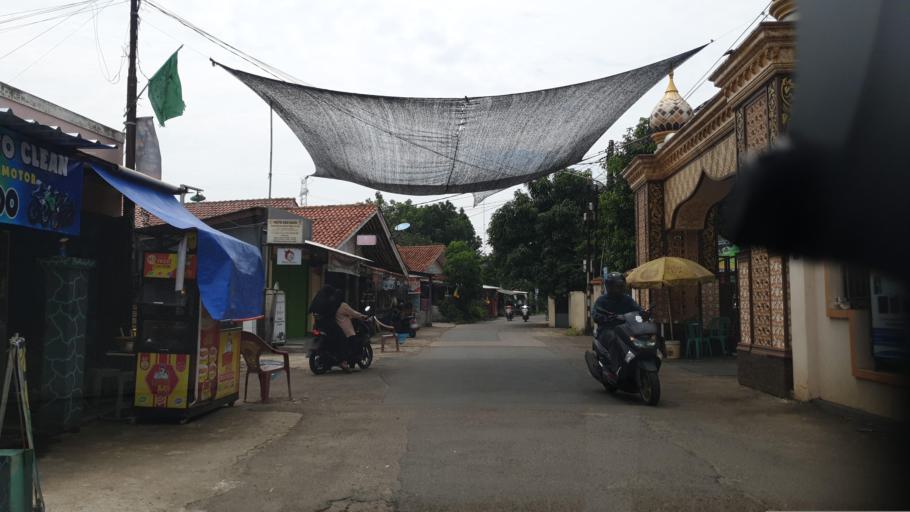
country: ID
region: West Java
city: Sawangan
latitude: -6.3773
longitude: 106.7603
